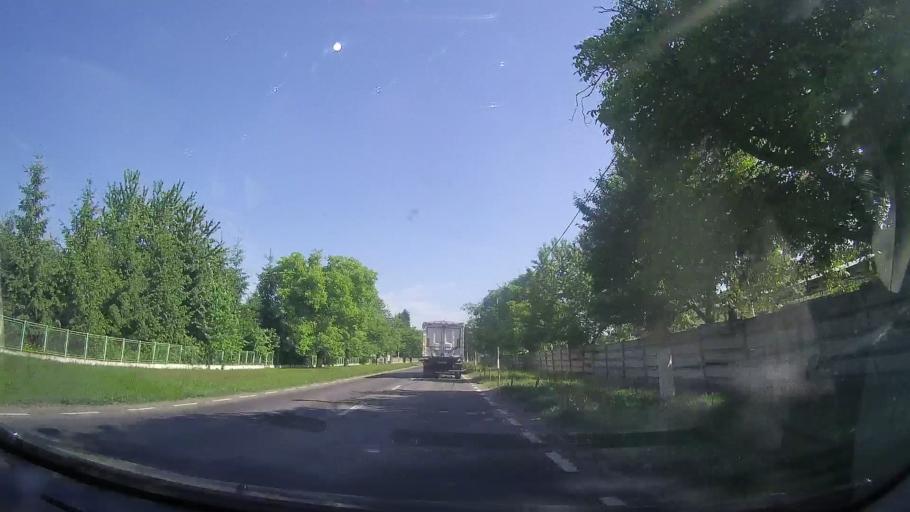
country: RO
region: Prahova
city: Drajna de Jos
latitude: 45.2132
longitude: 26.0383
